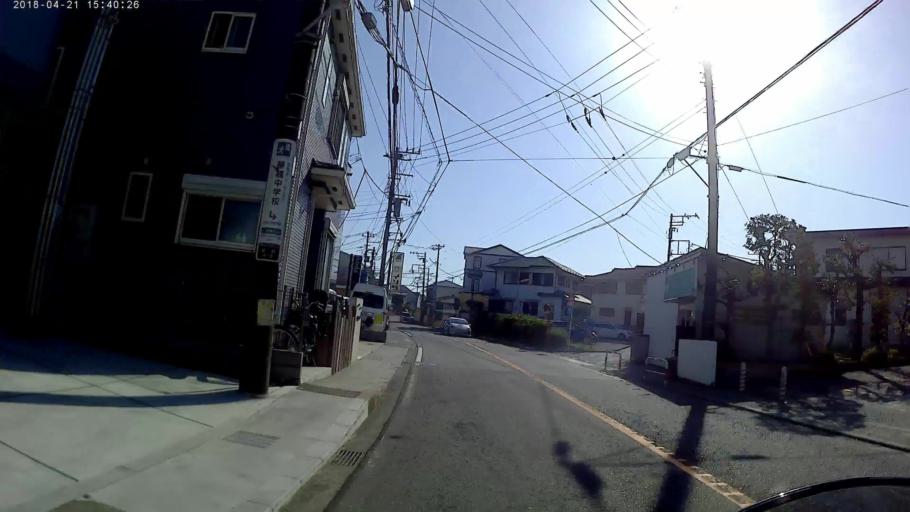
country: JP
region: Kanagawa
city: Fujisawa
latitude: 35.3112
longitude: 139.4974
